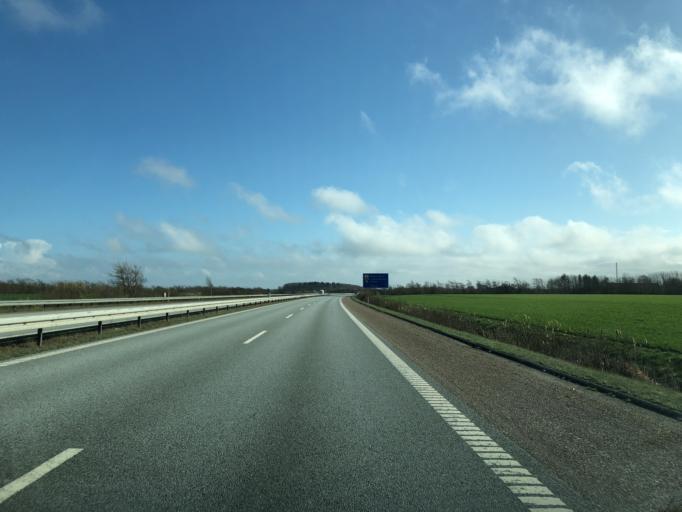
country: DK
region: North Denmark
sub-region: Hjorring Kommune
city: Hjorring
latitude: 57.4666
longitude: 10.0459
